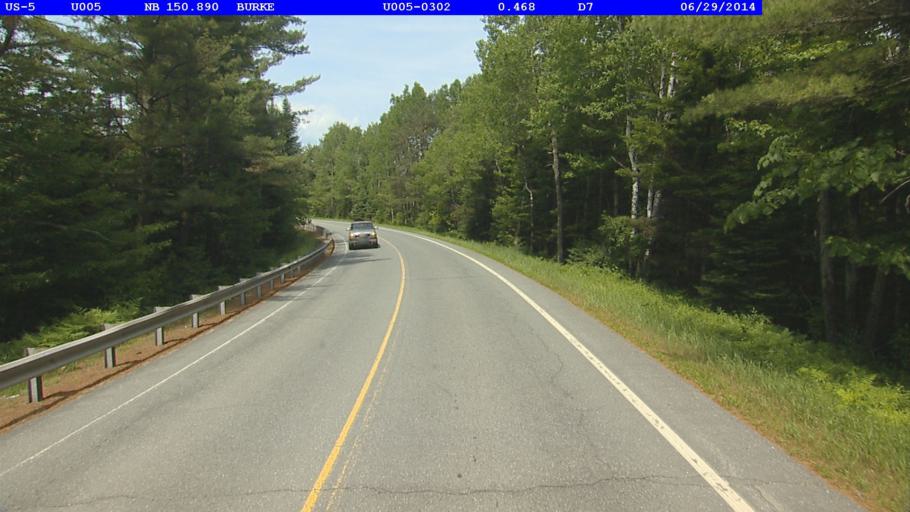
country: US
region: Vermont
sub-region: Caledonia County
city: Lyndonville
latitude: 44.5925
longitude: -71.9757
